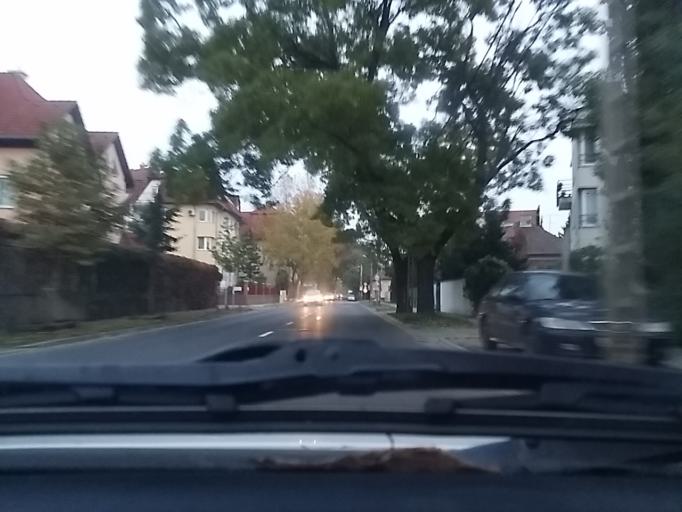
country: HU
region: Budapest
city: Budapest XIV. keruelet
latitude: 47.5313
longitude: 19.1201
